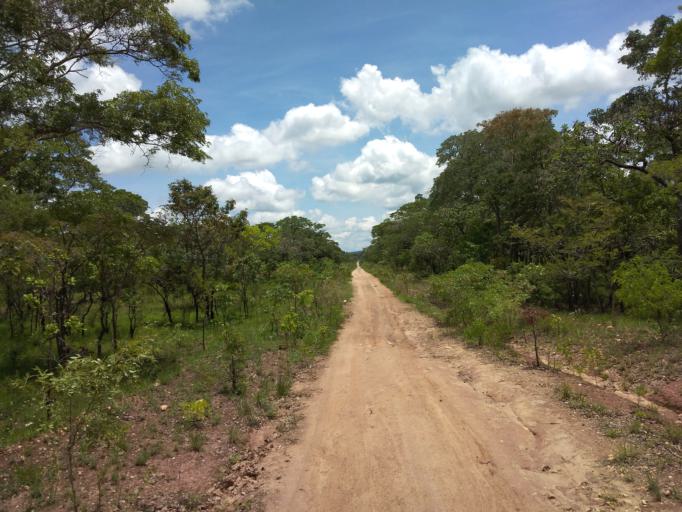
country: ZM
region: Central
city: Mkushi
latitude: -13.9410
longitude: 29.8671
